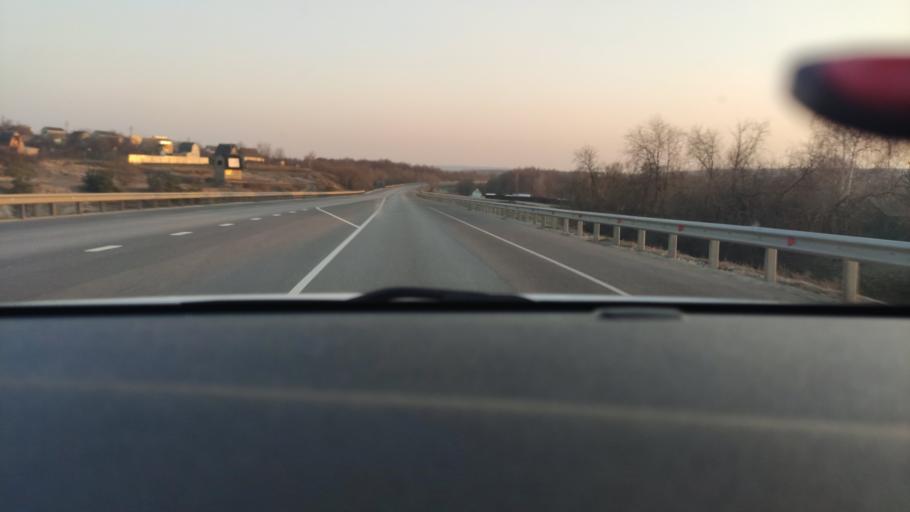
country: RU
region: Voronezj
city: Kolodeznyy
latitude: 51.3492
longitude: 39.1736
